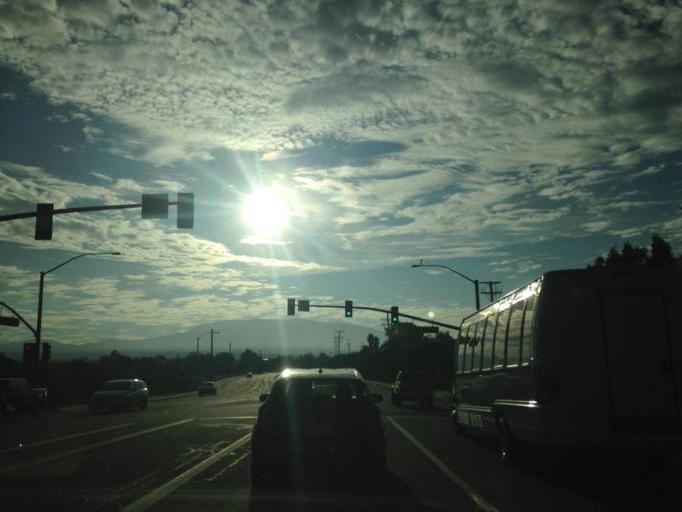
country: US
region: California
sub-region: Riverside County
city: Temecula
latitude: 33.4736
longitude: -117.1275
